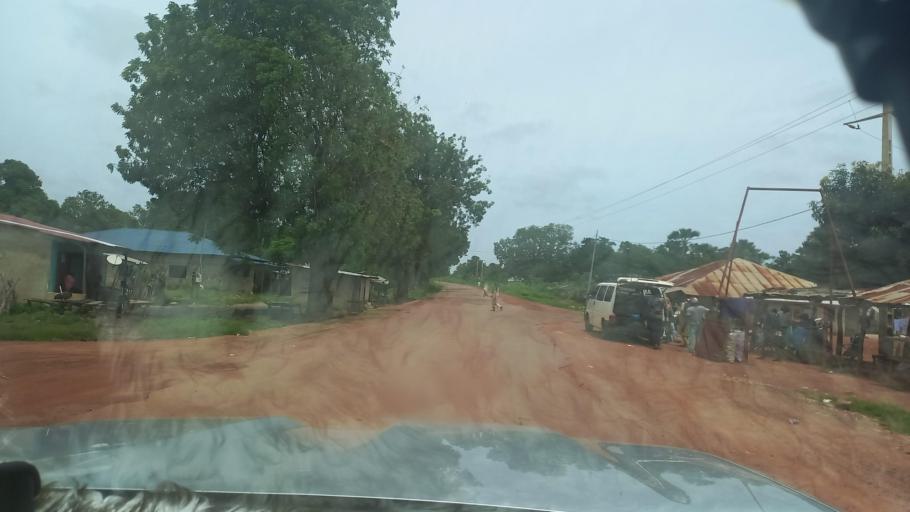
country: SN
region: Kolda
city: Marsassoum
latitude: 12.9142
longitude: -16.0100
